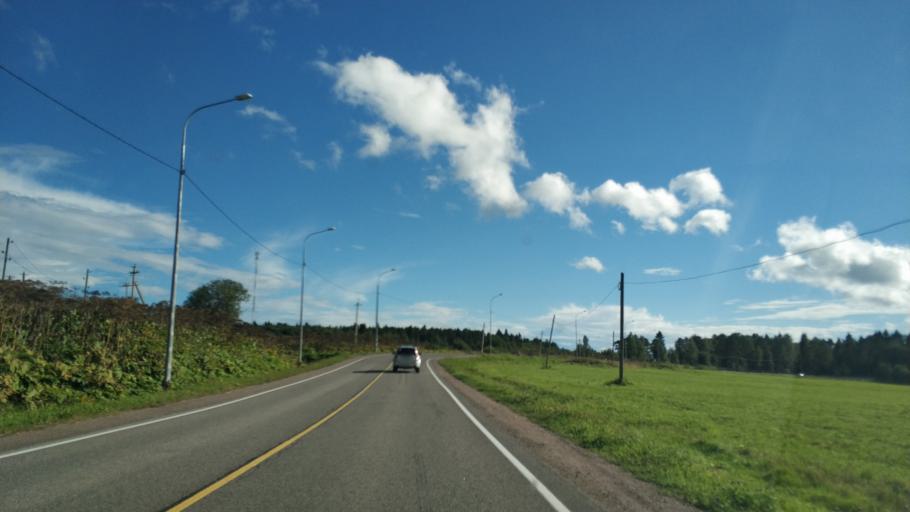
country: RU
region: Republic of Karelia
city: Khelyulya
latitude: 61.6442
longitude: 30.5830
